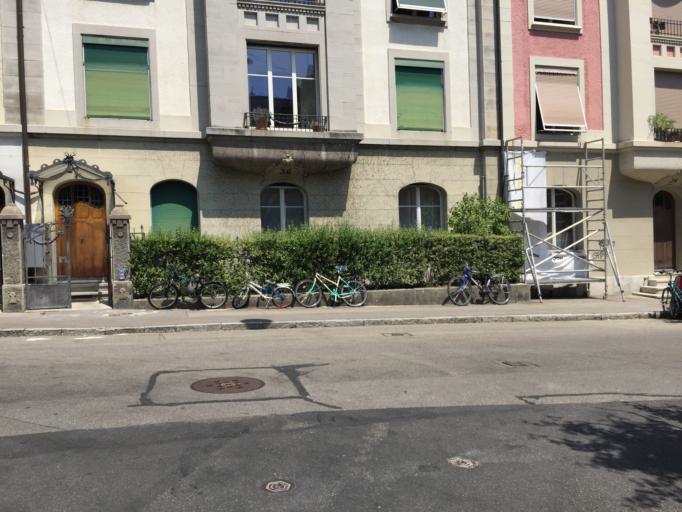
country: CH
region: Bern
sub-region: Bern-Mittelland District
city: Bern
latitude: 46.9576
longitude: 7.4557
